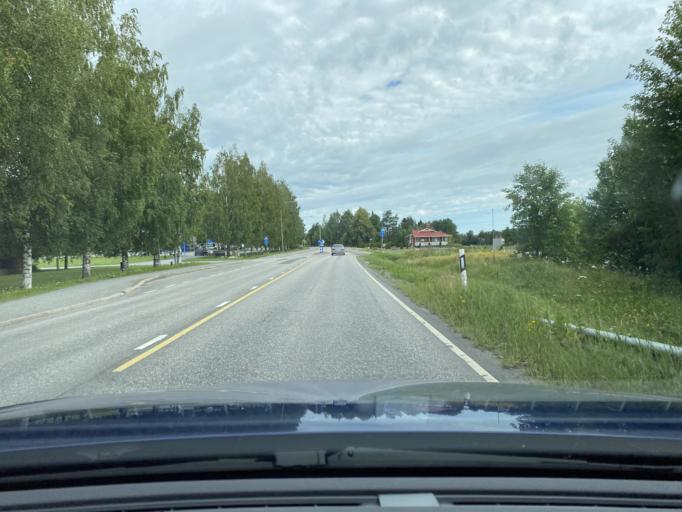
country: FI
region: Ostrobothnia
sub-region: Vaasa
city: Vaehaekyroe
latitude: 63.0470
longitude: 22.1162
